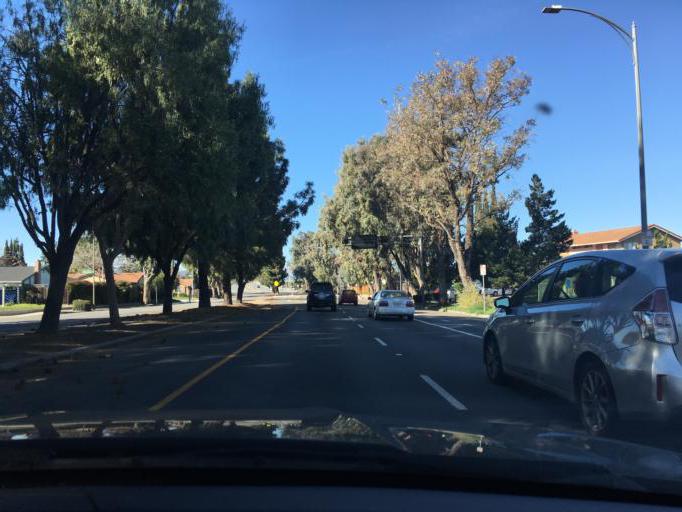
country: US
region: California
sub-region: Santa Clara County
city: Seven Trees
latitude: 37.2658
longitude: -121.8528
